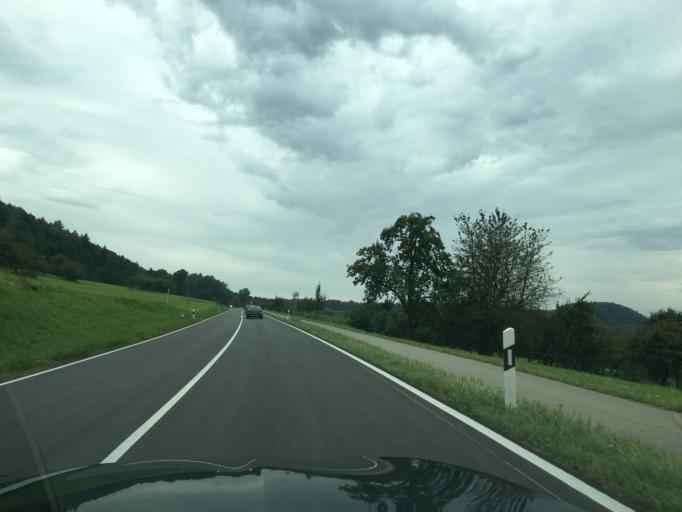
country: DE
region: Baden-Wuerttemberg
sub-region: Freiburg Region
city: Steisslingen
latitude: 47.7900
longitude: 8.9795
